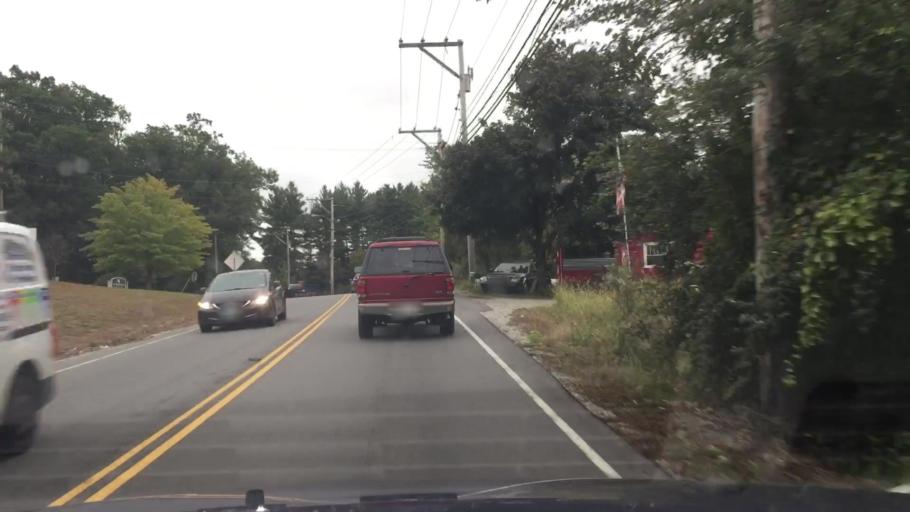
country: US
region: Massachusetts
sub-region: Middlesex County
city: Tyngsboro
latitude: 42.7184
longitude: -71.4176
